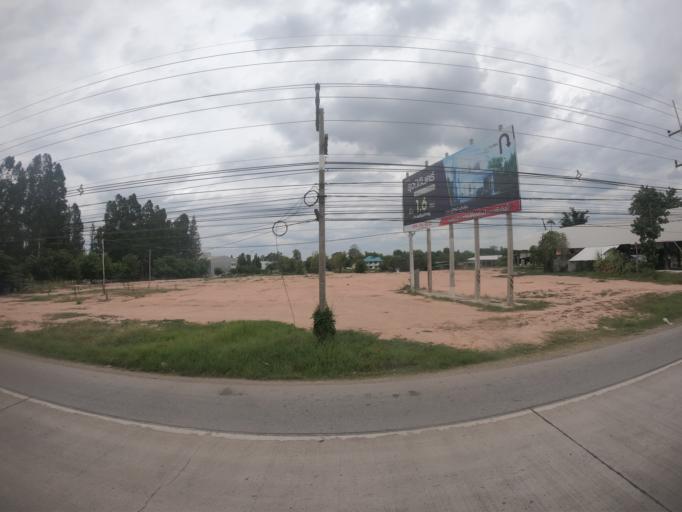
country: TH
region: Nakhon Ratchasima
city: Chok Chai
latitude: 14.8006
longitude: 102.1715
